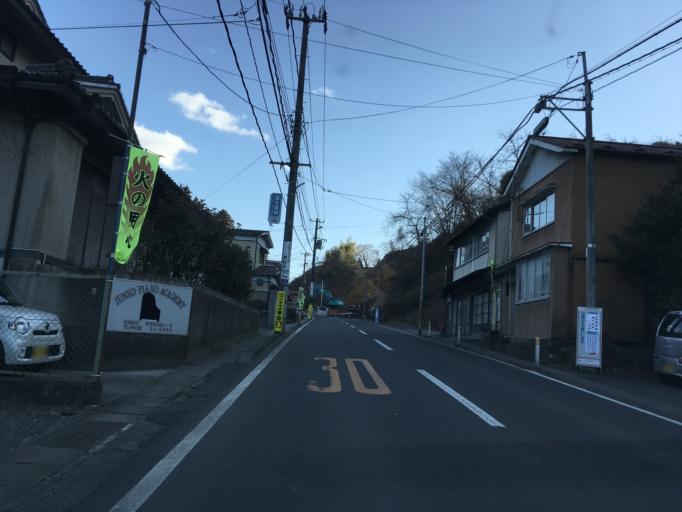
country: JP
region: Iwate
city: Ofunato
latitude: 38.9050
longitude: 141.5644
